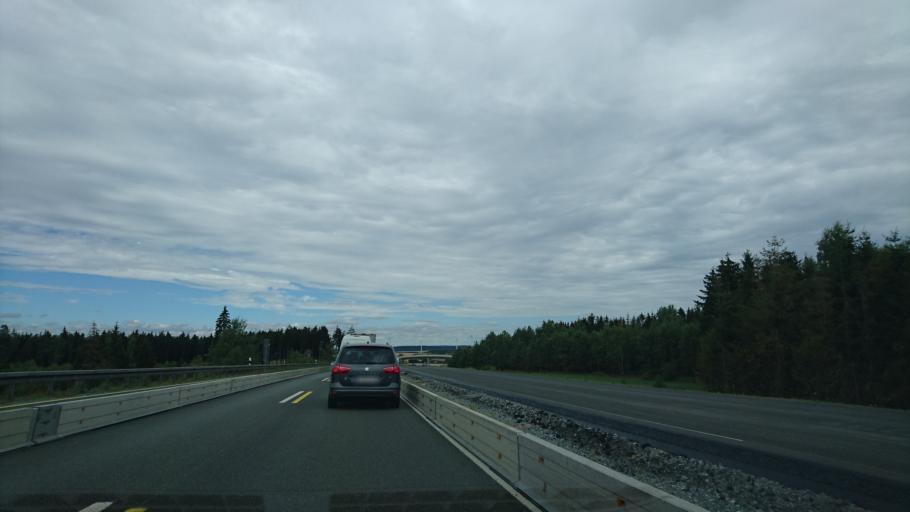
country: DE
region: Bavaria
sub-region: Upper Franconia
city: Rehau
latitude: 50.2724
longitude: 12.0270
